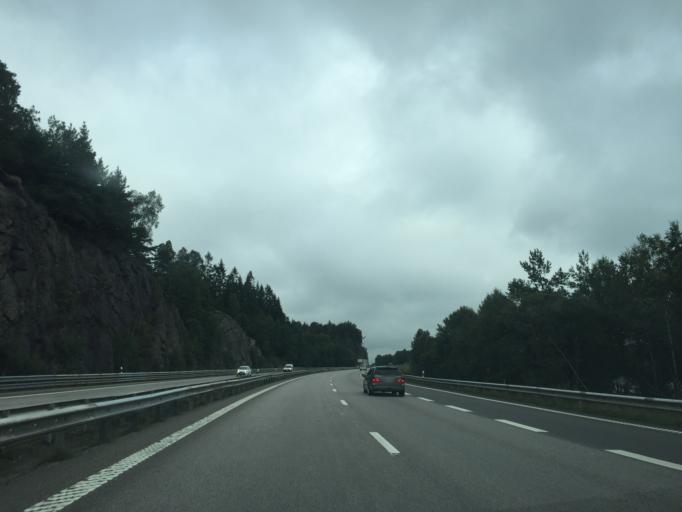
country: SE
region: Halland
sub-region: Kungsbacka Kommun
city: Fjaeras kyrkby
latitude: 57.3900
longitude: 12.1893
